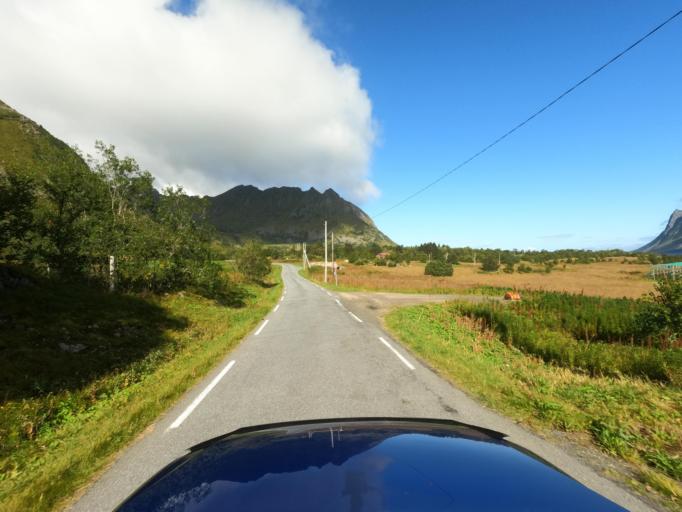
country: NO
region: Nordland
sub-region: Vagan
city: Kabelvag
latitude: 68.2839
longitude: 14.2664
